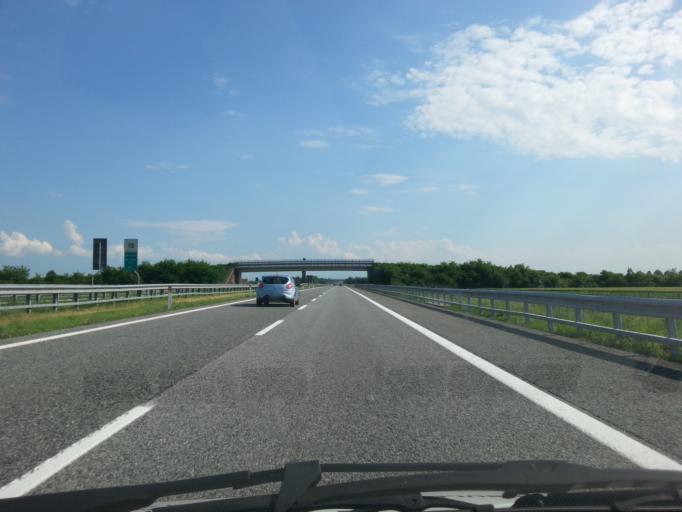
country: IT
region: Piedmont
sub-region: Provincia di Torino
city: Carmagnola
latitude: 44.8363
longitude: 7.7496
